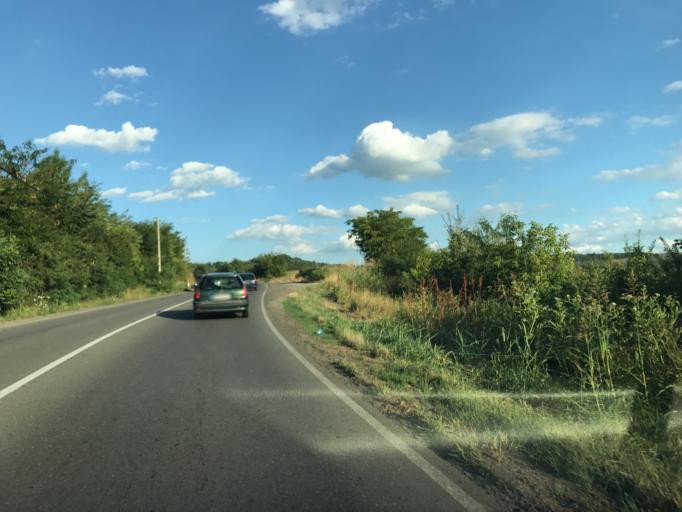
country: RS
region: Central Serbia
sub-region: Belgrade
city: Grocka
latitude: 44.7177
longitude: 20.6515
